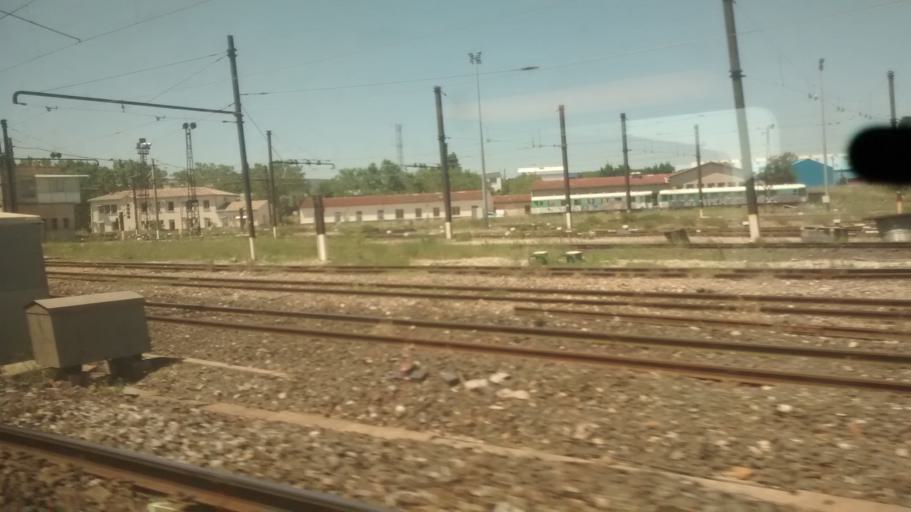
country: FR
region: Languedoc-Roussillon
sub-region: Departement du Gard
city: Rodilhan
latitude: 43.8474
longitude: 4.4029
